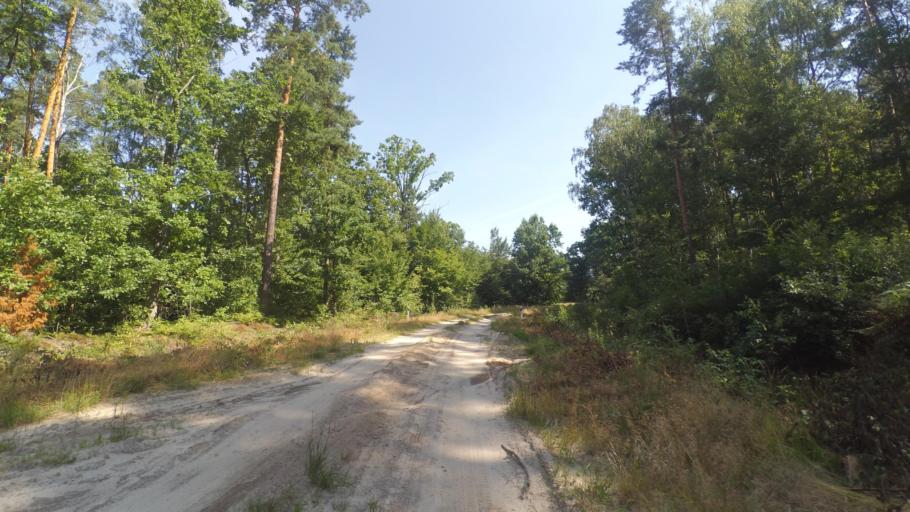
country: PL
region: Lublin Voivodeship
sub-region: Powiat wlodawski
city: Wlodawa
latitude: 51.6172
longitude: 23.6447
